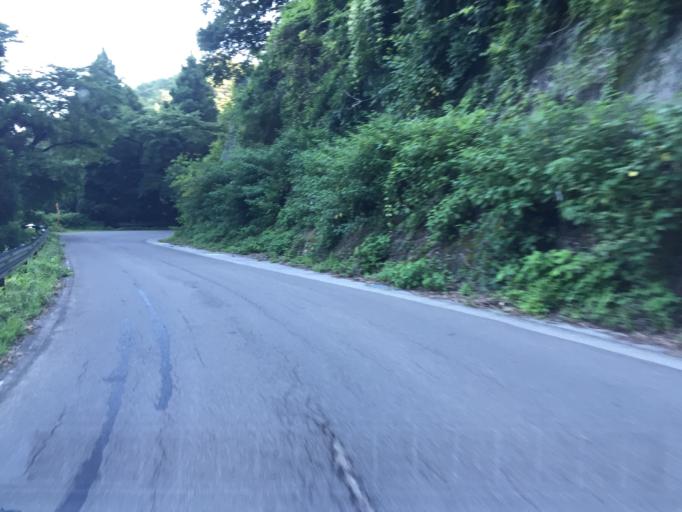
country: JP
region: Fukushima
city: Hobaramachi
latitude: 37.9027
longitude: 140.5120
